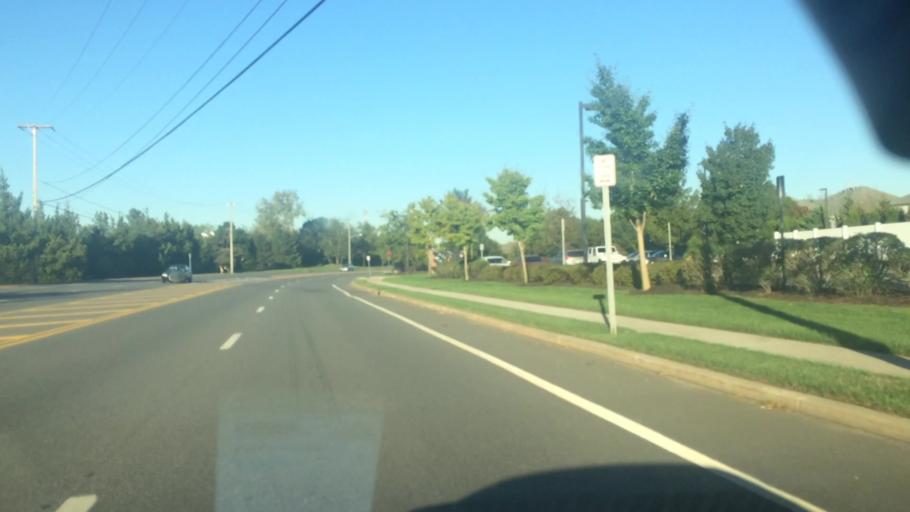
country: US
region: New Jersey
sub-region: Ocean County
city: Toms River
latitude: 39.9864
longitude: -74.1981
